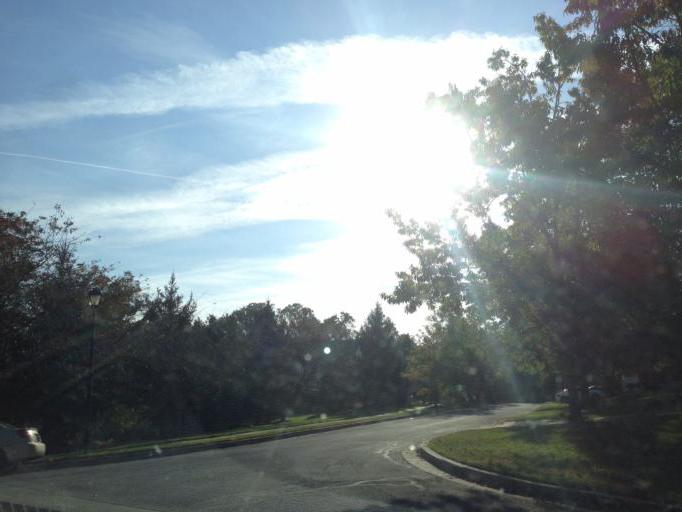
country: US
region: Maryland
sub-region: Howard County
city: Ellicott City
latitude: 39.2808
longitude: -76.8002
